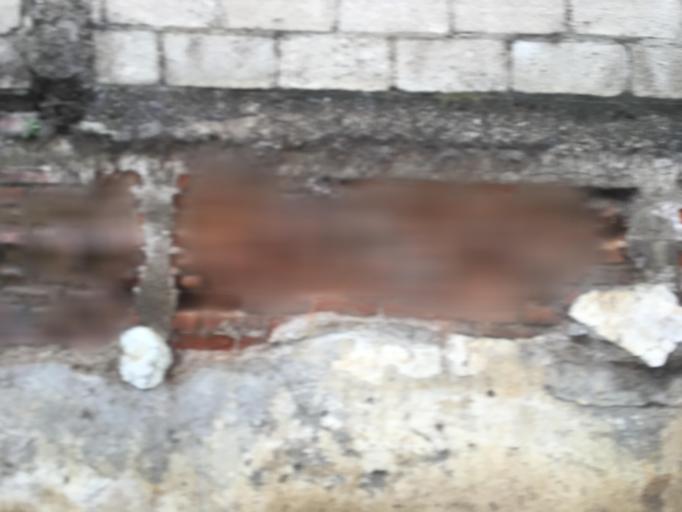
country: GT
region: Guatemala
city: Villa Canales
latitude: 14.4508
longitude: -90.5668
